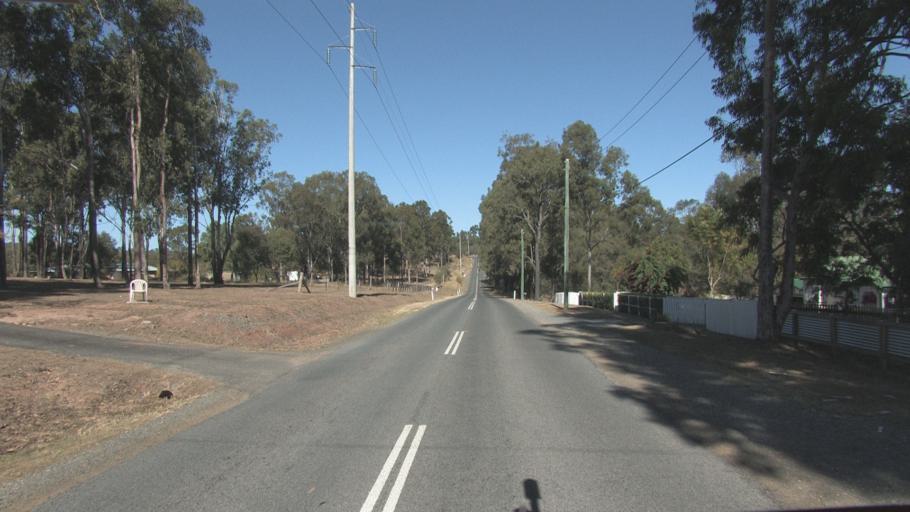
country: AU
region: Queensland
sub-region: Logan
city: Cedar Vale
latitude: -27.8776
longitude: 153.0162
